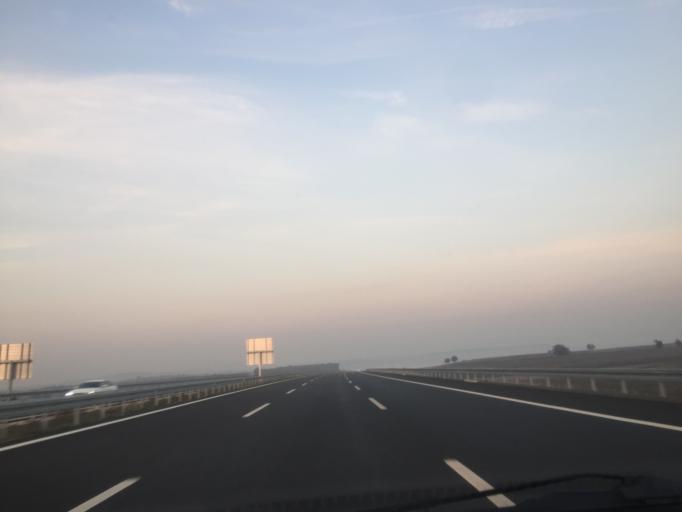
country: TR
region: Bursa
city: Mahmudiye
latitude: 40.2575
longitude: 28.6923
